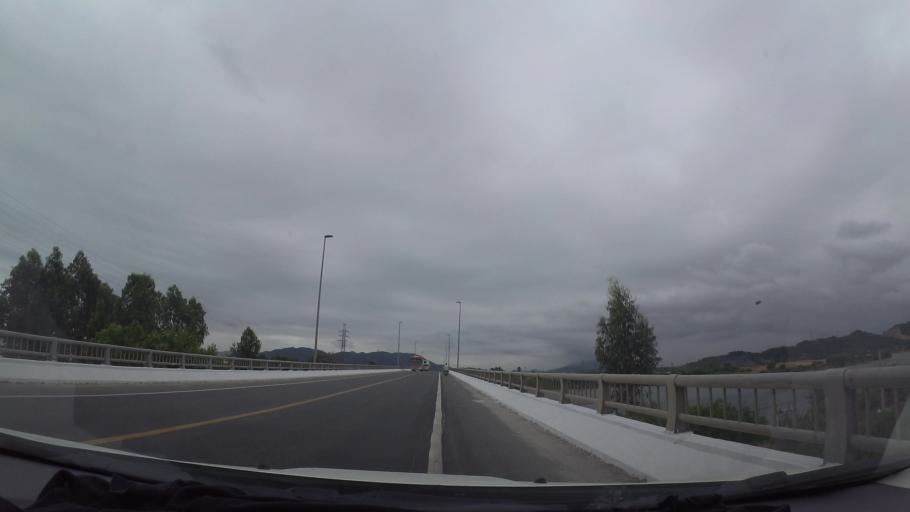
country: VN
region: Da Nang
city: Lien Chieu
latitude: 16.1161
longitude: 108.1042
